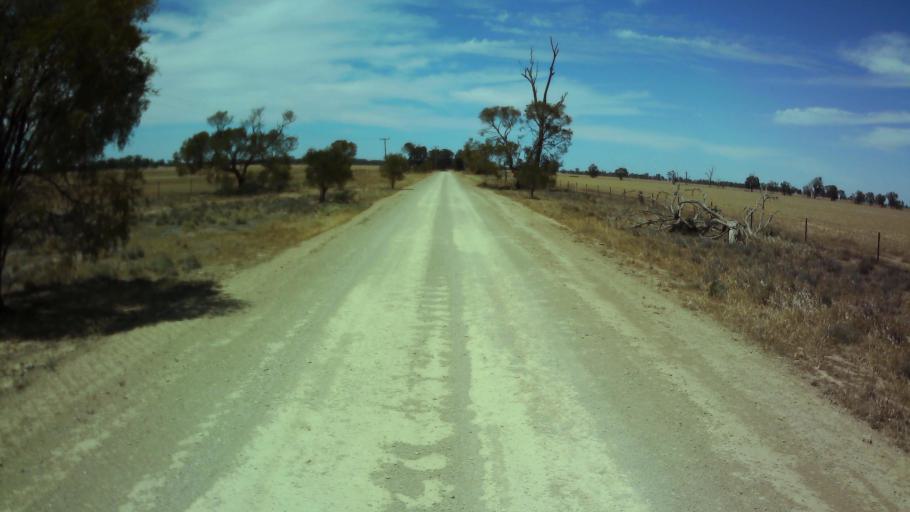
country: AU
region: New South Wales
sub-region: Weddin
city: Grenfell
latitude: -33.8816
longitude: 147.8044
